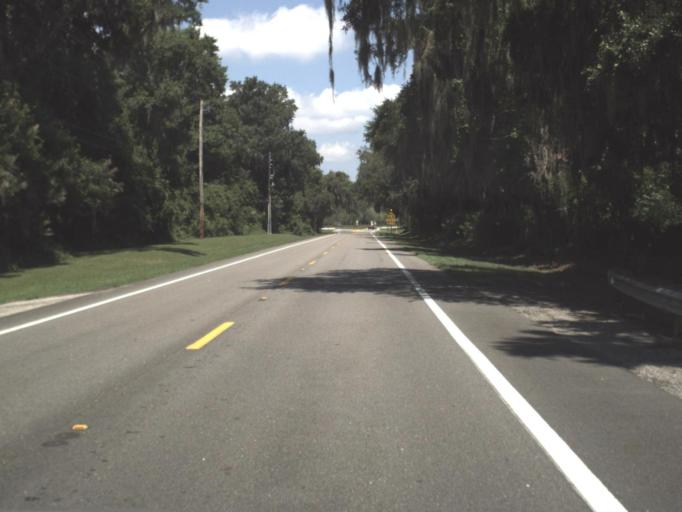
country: US
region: Florida
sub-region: Clay County
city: Green Cove Springs
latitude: 30.0188
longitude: -81.6355
